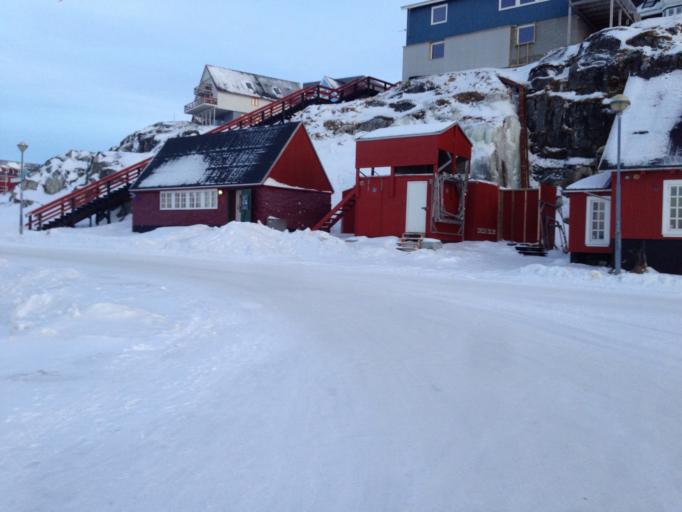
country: GL
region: Sermersooq
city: Nuuk
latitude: 64.1768
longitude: -51.7465
